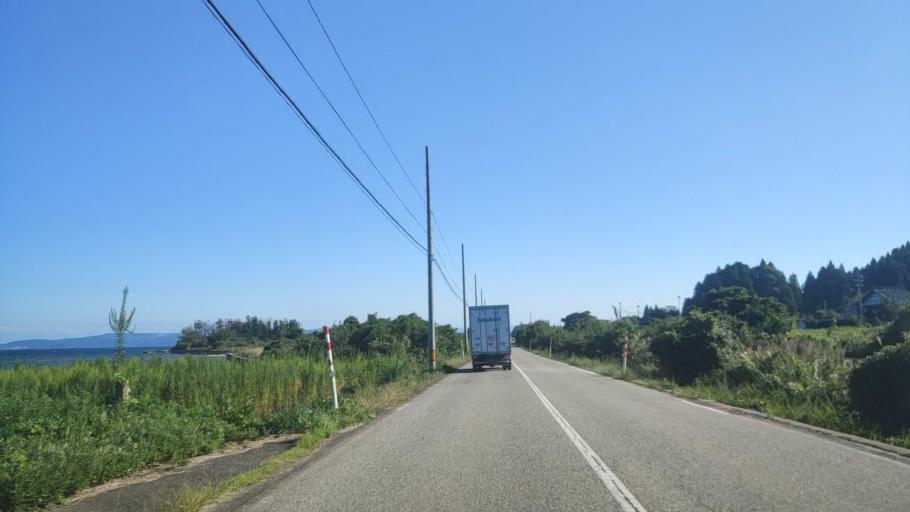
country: JP
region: Ishikawa
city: Nanao
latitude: 37.1972
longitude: 136.9101
